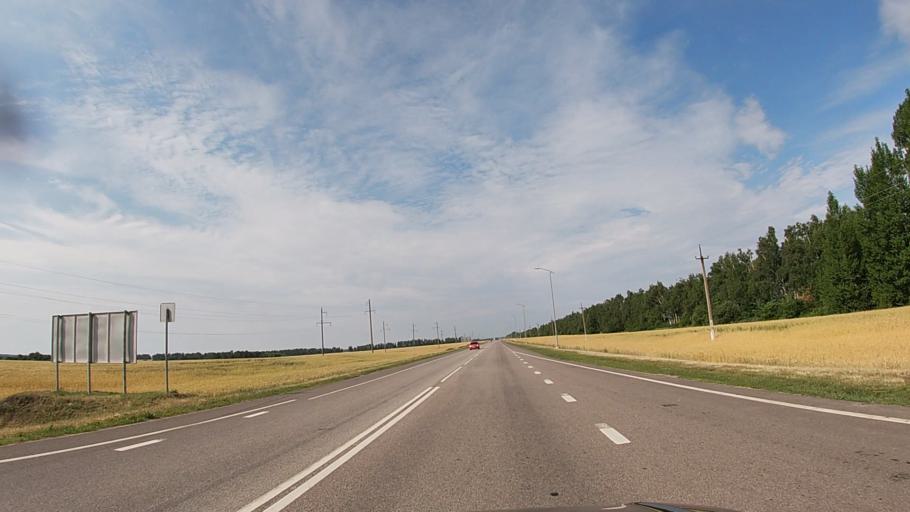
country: RU
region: Belgorod
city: Proletarskiy
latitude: 50.8301
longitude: 35.7655
